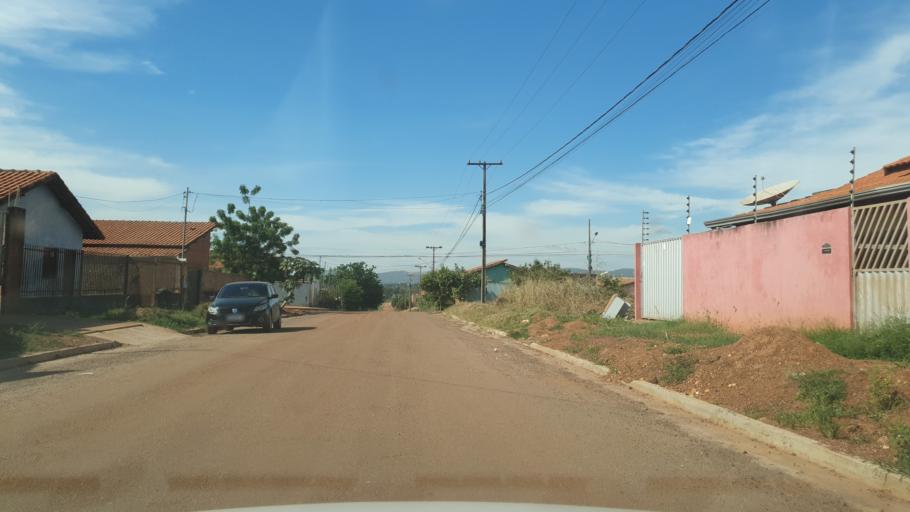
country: BR
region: Mato Grosso
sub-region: Pontes E Lacerda
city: Pontes e Lacerda
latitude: -15.2491
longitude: -59.3152
